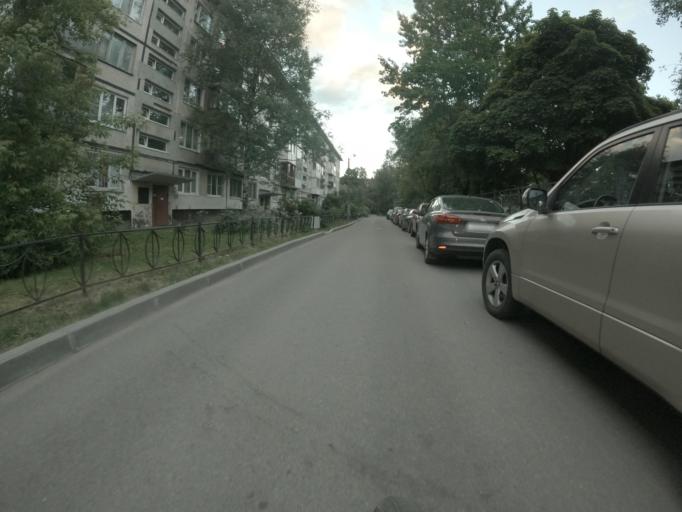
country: RU
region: St.-Petersburg
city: Kupchino
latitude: 59.8544
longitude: 30.3787
